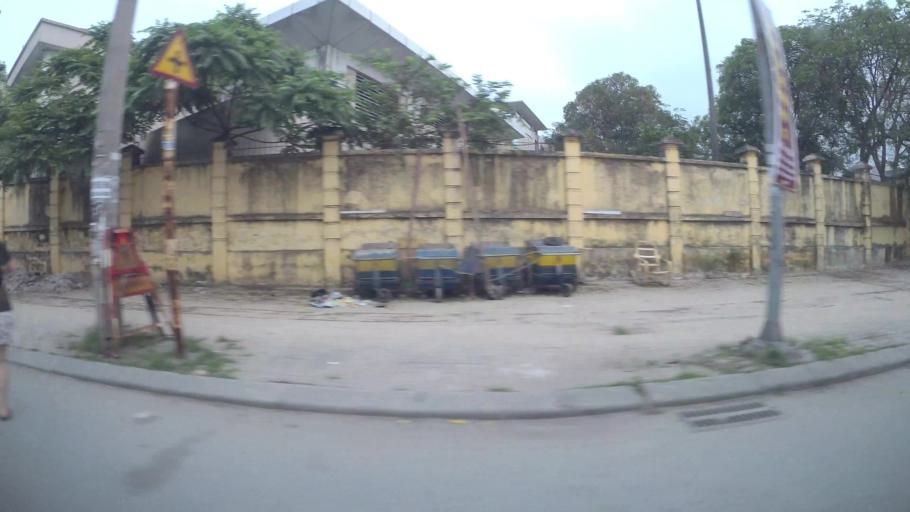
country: VN
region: Ha Noi
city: Hoan Kiem
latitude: 21.0559
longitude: 105.8961
